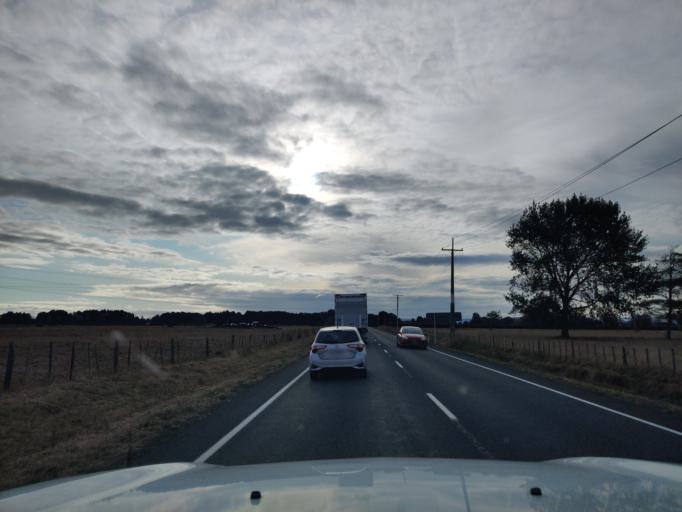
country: NZ
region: Waikato
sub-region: Hamilton City
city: Hamilton
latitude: -37.6859
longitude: 175.3364
